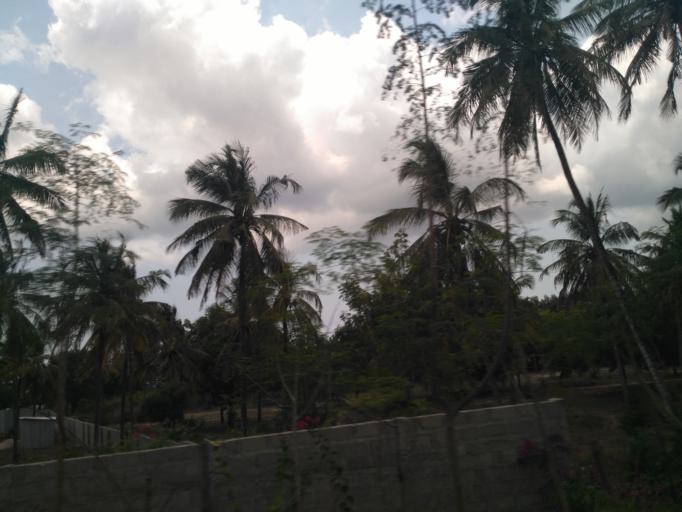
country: TZ
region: Dar es Salaam
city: Dar es Salaam
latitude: -6.8505
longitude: 39.3564
